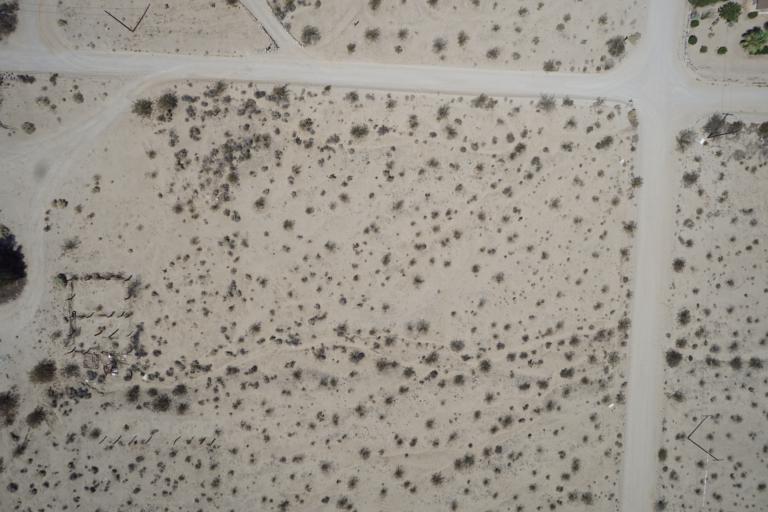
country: US
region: California
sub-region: San Bernardino County
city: Twentynine Palms
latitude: 34.1281
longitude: -116.0297
